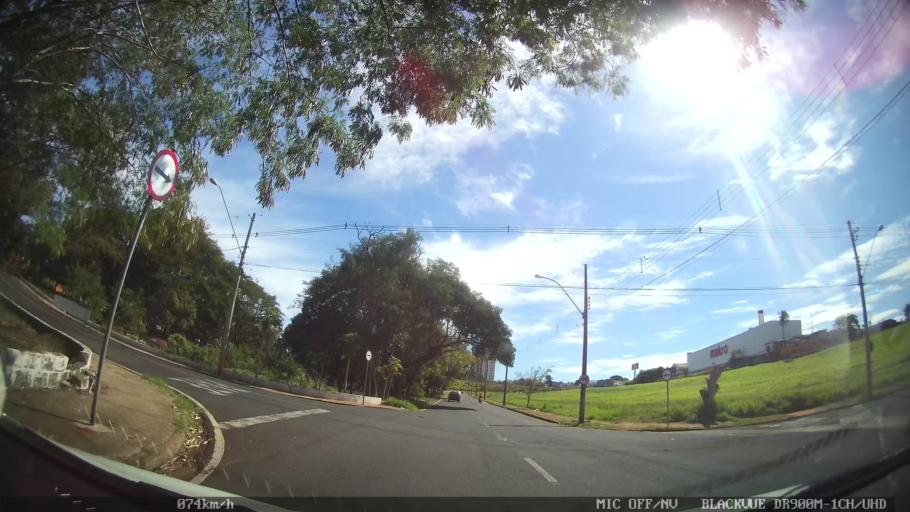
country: BR
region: Sao Paulo
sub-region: Sao Jose Do Rio Preto
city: Sao Jose do Rio Preto
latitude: -20.8392
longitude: -49.3656
